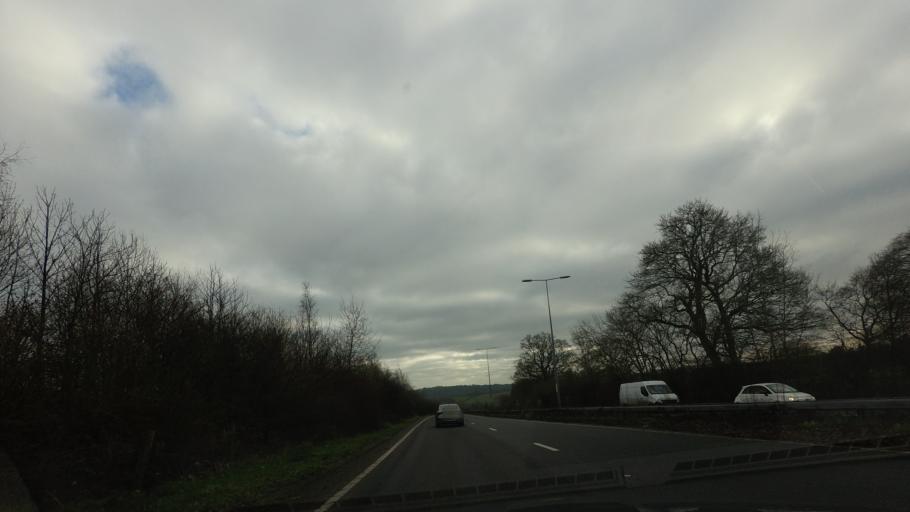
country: GB
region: England
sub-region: Kent
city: Paddock Wood
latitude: 51.1101
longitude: 0.4020
